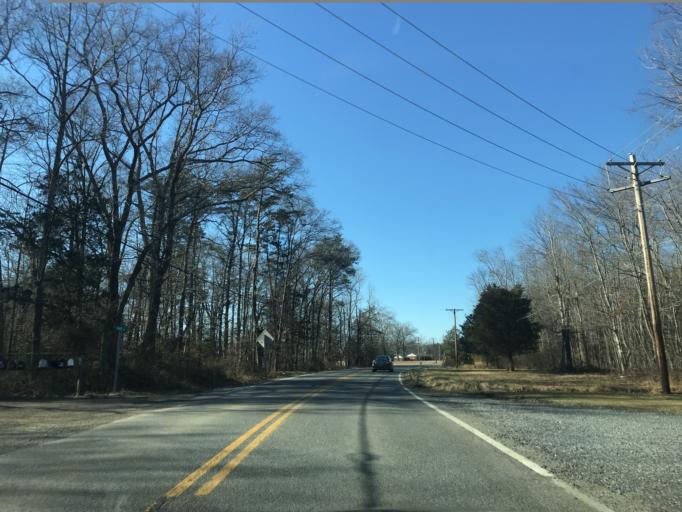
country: US
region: Maryland
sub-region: Charles County
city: Bryans Road
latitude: 38.6022
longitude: -77.0633
